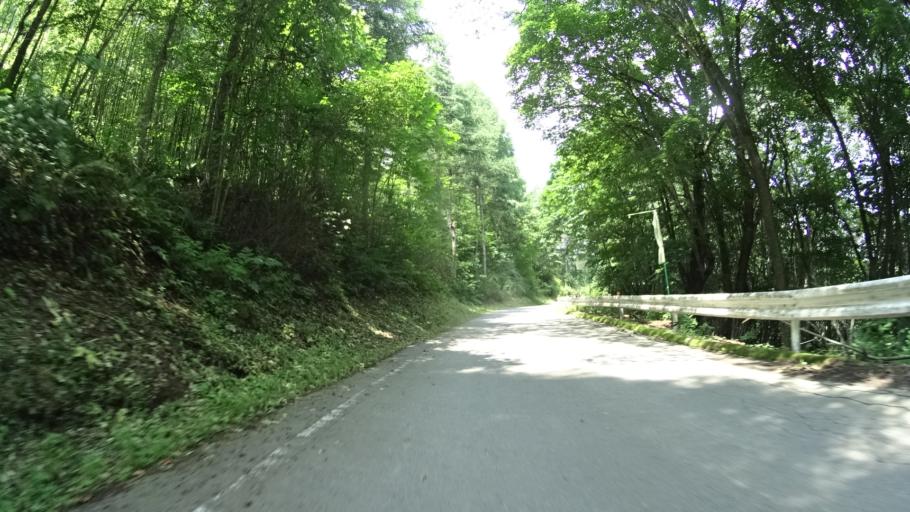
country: JP
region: Nagano
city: Saku
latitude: 36.1014
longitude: 138.6504
